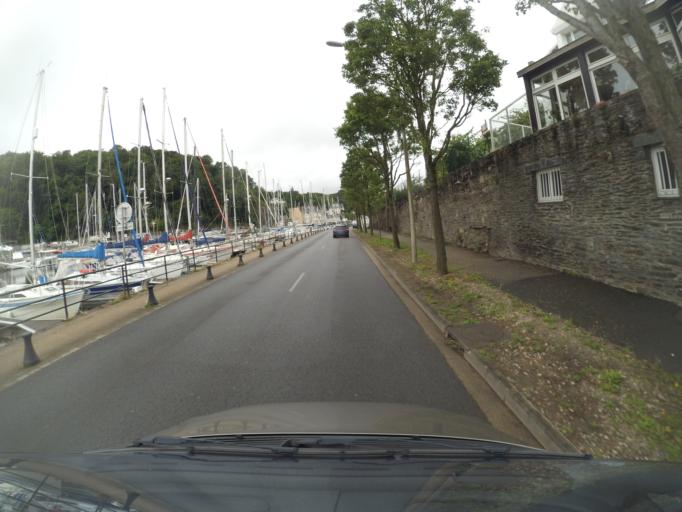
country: FR
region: Brittany
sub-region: Departement du Finistere
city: Morlaix
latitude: 48.5856
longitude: -3.8354
